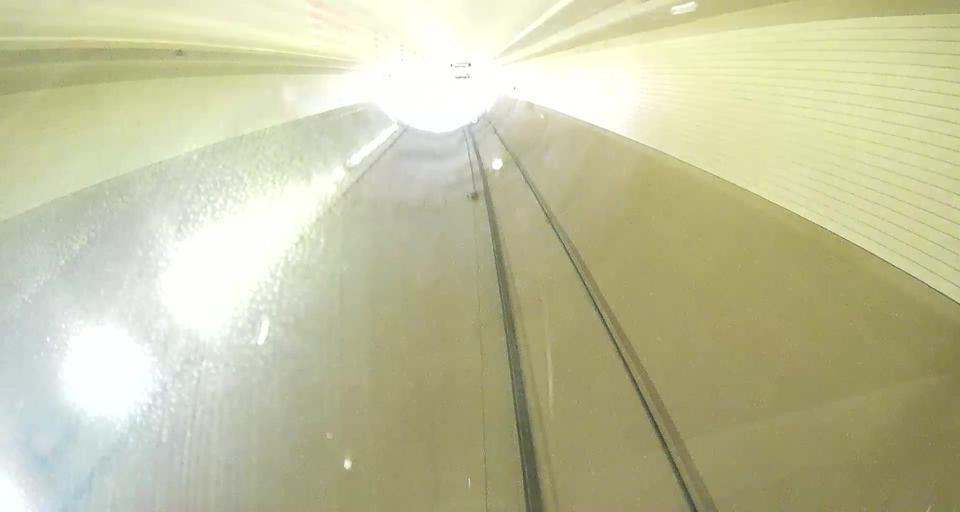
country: JP
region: Iwate
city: Miyako
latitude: 39.9327
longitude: 141.8484
